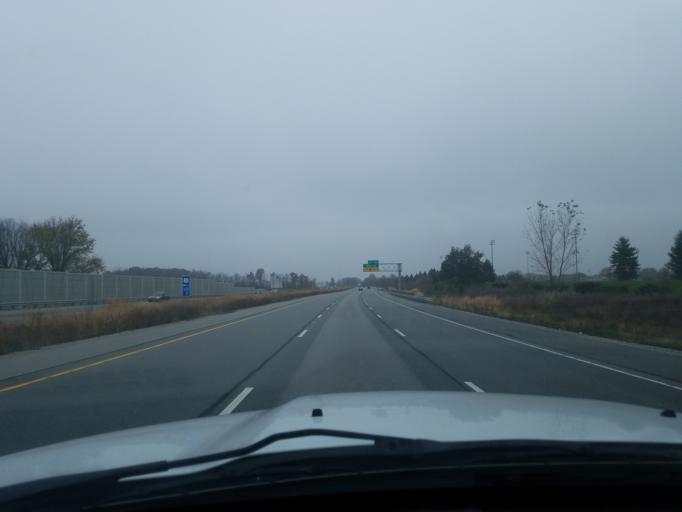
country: US
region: Indiana
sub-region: Hamilton County
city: Westfield
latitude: 40.0529
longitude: -86.1328
